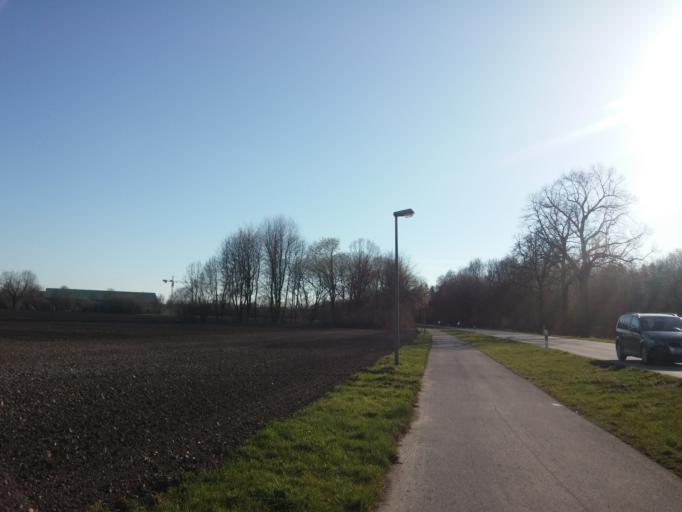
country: DE
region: Bavaria
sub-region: Upper Bavaria
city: Ismaning
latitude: 48.2454
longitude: 11.6873
